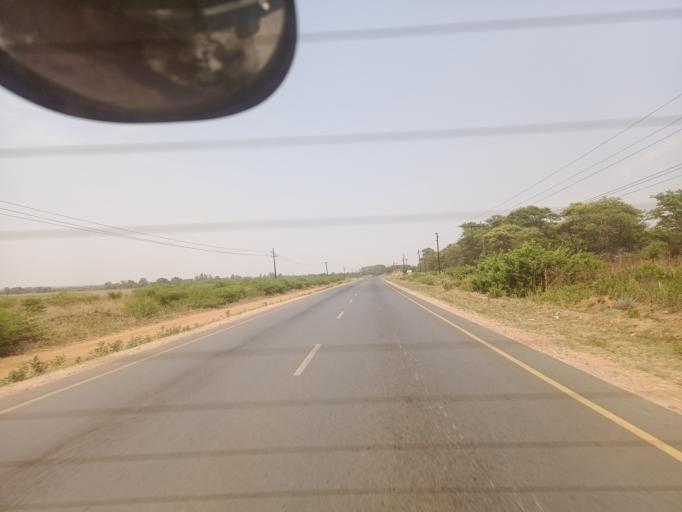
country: ZM
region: Lusaka
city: Lusaka
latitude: -15.2694
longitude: 28.4147
